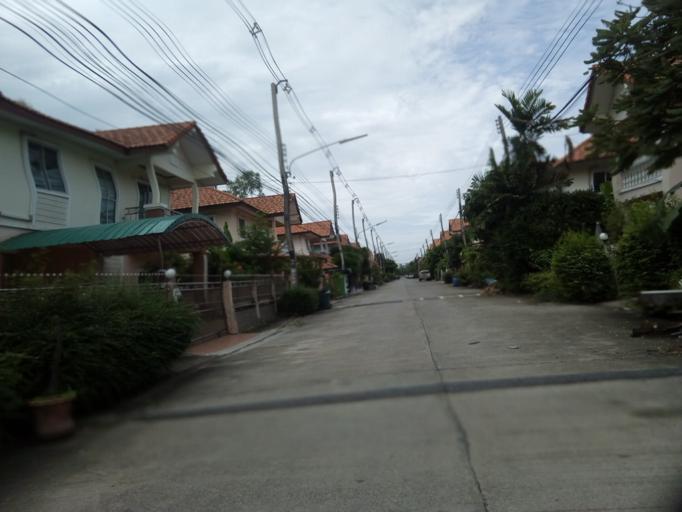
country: TH
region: Pathum Thani
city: Nong Suea
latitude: 14.0535
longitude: 100.8352
